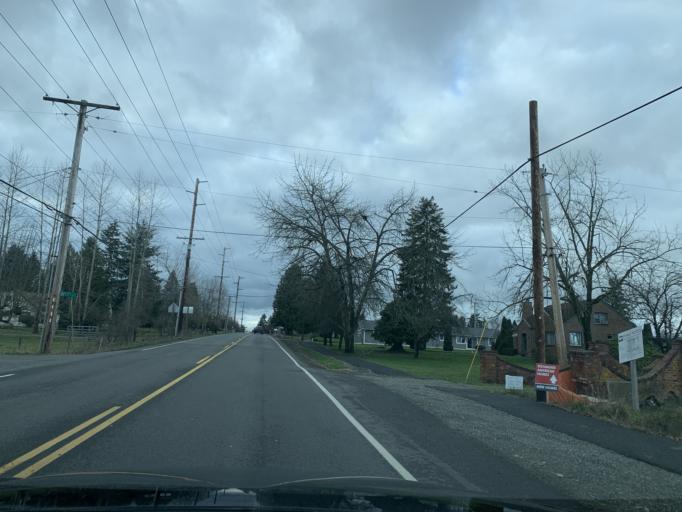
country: US
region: Washington
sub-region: Pierce County
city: Edgewood
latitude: 47.2356
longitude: -122.3010
